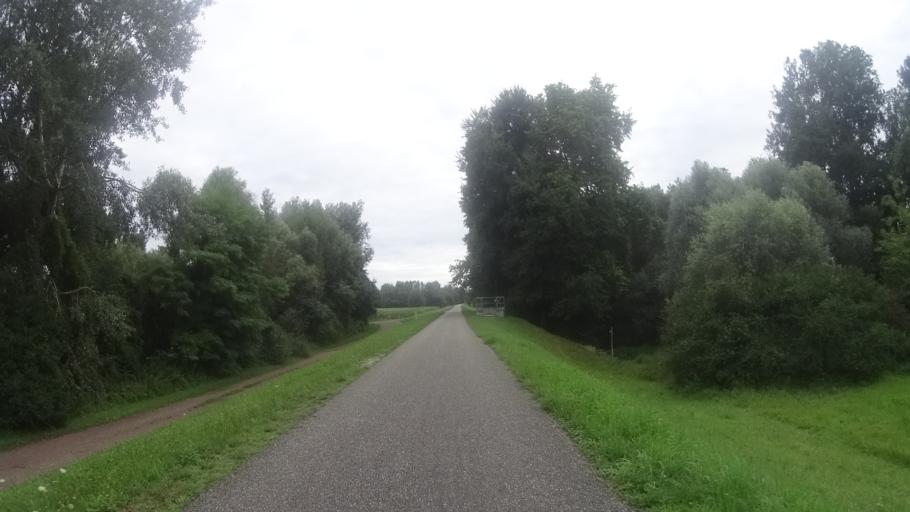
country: FR
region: Alsace
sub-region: Departement du Bas-Rhin
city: Seltz
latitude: 48.8790
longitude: 8.1248
